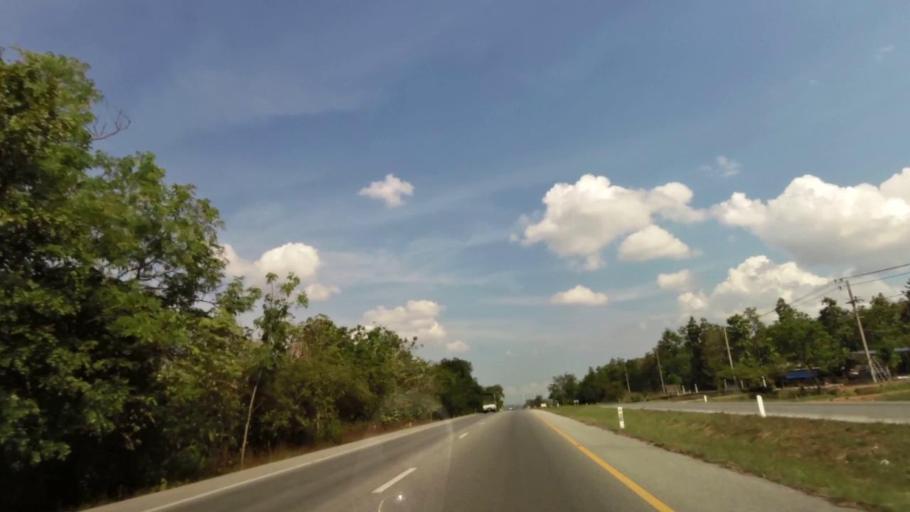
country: TH
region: Uttaradit
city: Thong Saen Khan
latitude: 17.4484
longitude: 100.2351
